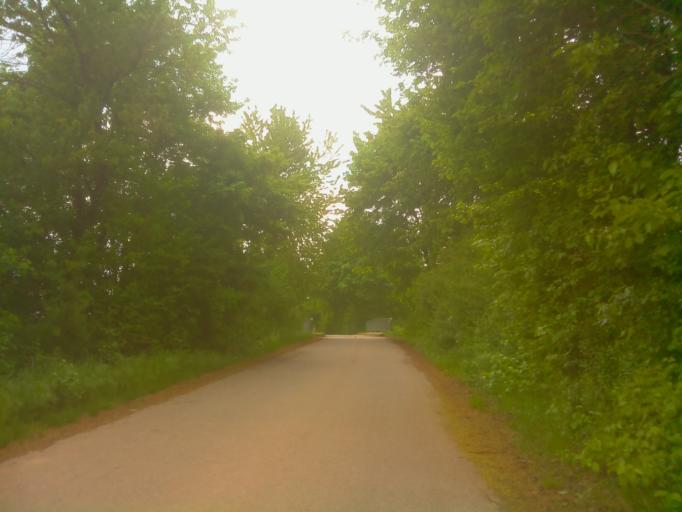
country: DE
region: Baden-Wuerttemberg
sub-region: Karlsruhe Region
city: Oftersheim
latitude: 49.3653
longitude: 8.6087
